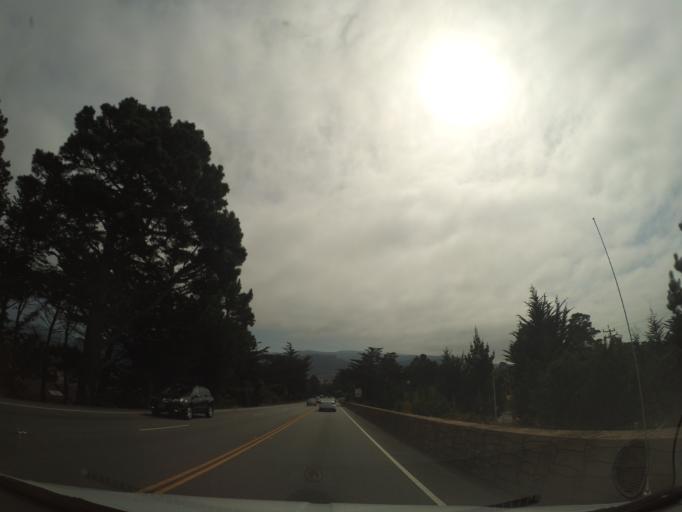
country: US
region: California
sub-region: Monterey County
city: Carmel-by-the-Sea
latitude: 36.5481
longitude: -121.9099
